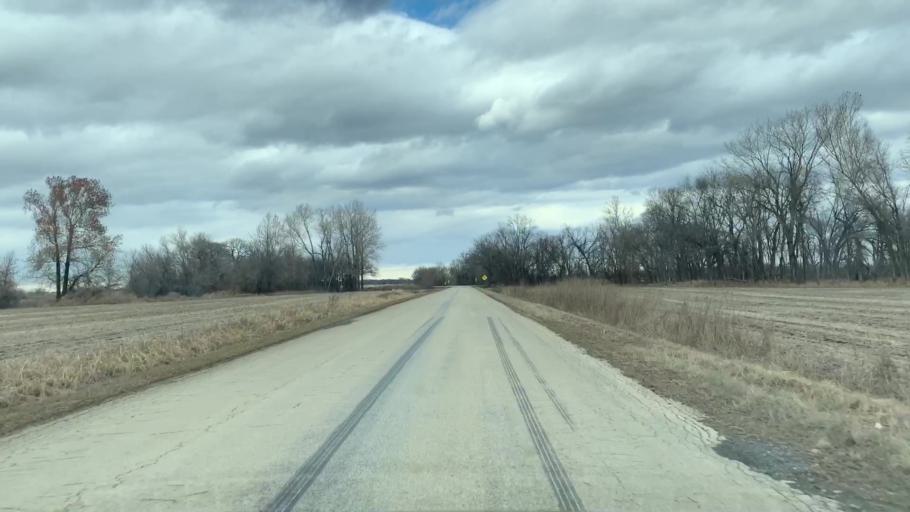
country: US
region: Kansas
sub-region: Allen County
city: Humboldt
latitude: 37.8077
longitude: -95.4712
